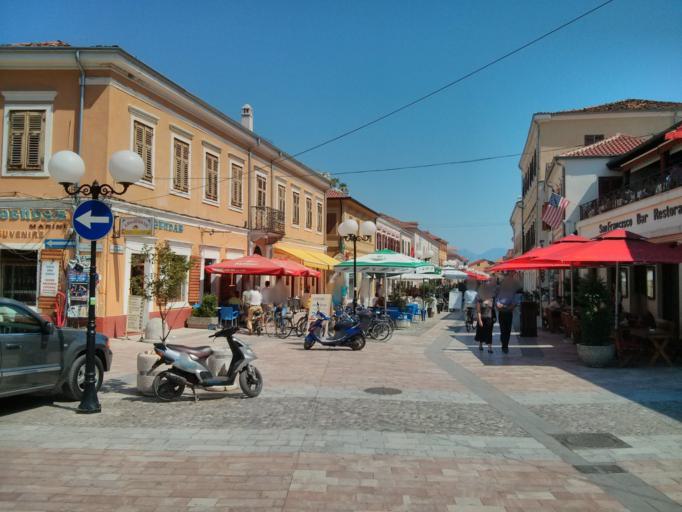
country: AL
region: Shkoder
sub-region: Rrethi i Shkodres
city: Shkoder
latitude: 42.0669
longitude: 19.5139
